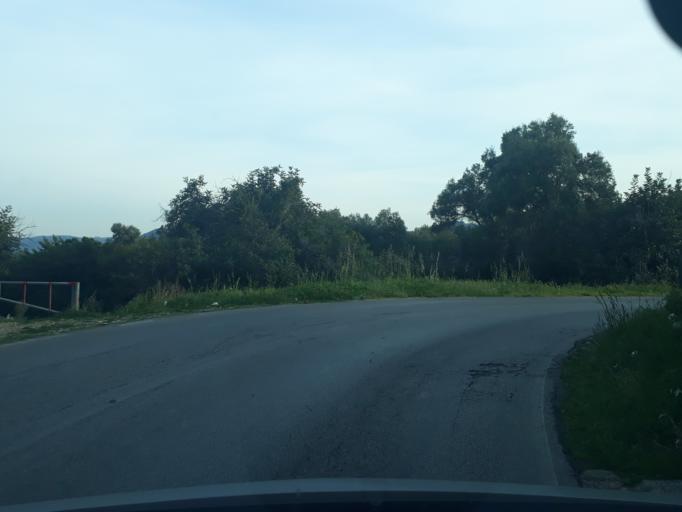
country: IT
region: Apulia
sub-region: Provincia di Brindisi
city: Fasano
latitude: 40.8331
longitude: 17.3451
